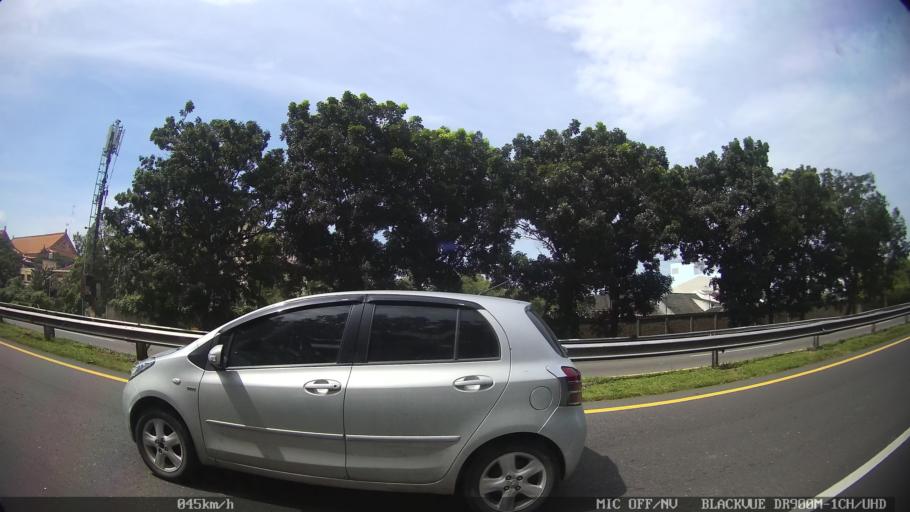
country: ID
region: North Sumatra
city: Medan
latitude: 3.6405
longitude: 98.6988
